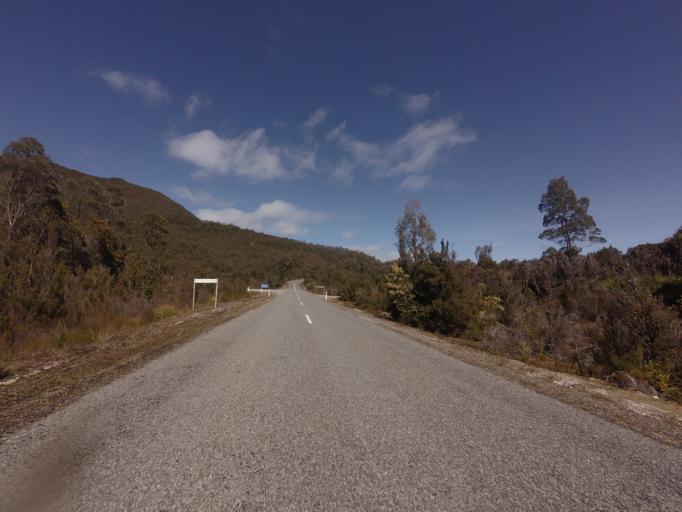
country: AU
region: Tasmania
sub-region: Huon Valley
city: Geeveston
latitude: -42.8138
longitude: 146.3863
